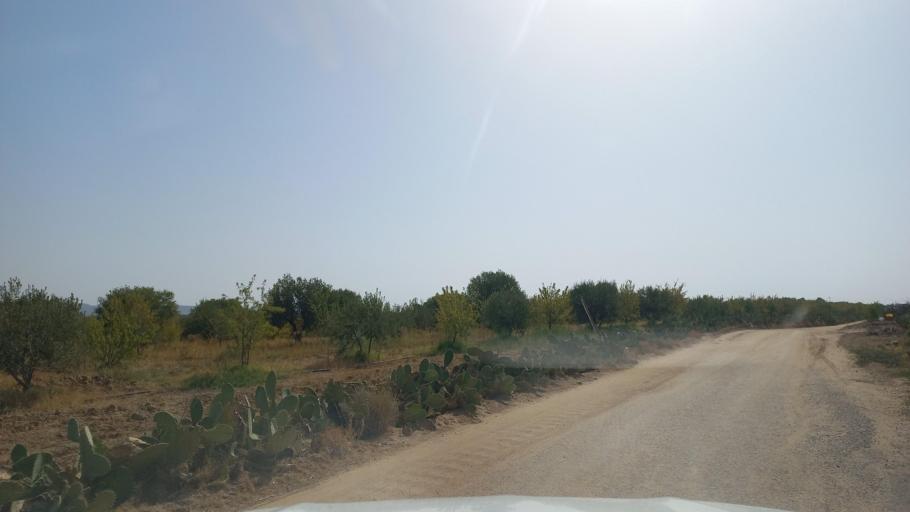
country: TN
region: Al Qasrayn
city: Kasserine
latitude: 35.2459
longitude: 9.0307
